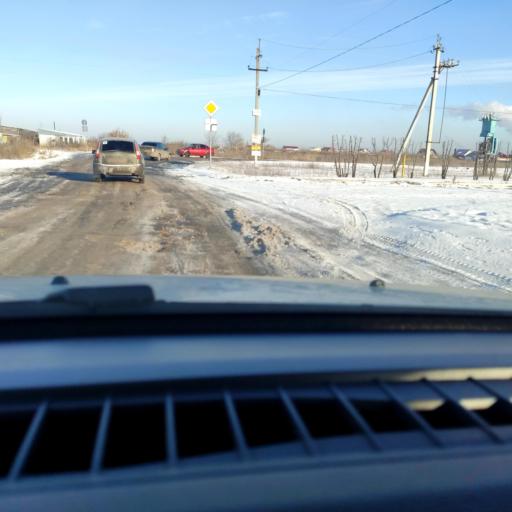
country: RU
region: Samara
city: Podstepki
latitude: 53.5225
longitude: 49.1459
